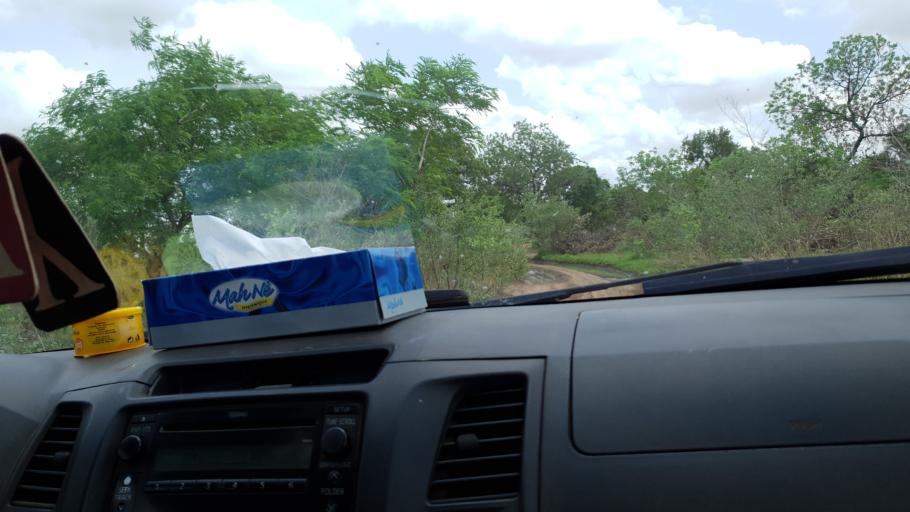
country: ML
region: Segou
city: Baroueli
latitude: 13.3498
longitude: -7.0953
